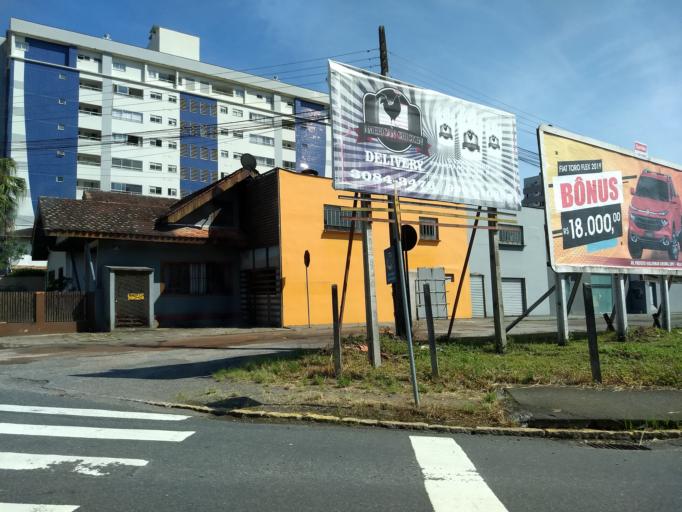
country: BR
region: Santa Catarina
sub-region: Jaragua Do Sul
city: Jaragua do Sul
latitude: -26.4918
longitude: -49.0747
